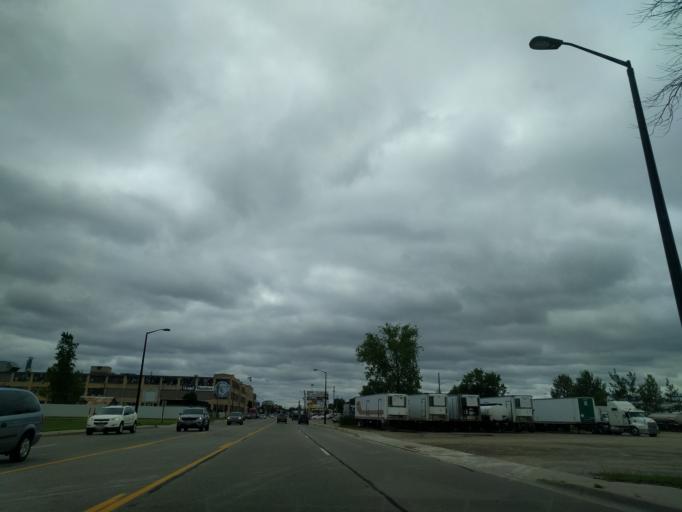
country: US
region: Michigan
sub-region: Menominee County
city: Menominee
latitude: 45.1289
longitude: -87.6129
